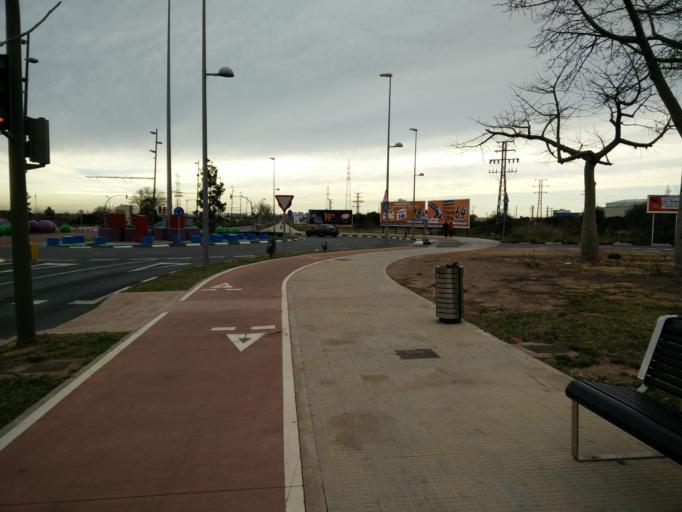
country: ES
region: Valencia
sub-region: Provincia de Castello
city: Castello de la Plana
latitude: 39.9823
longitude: -0.0180
